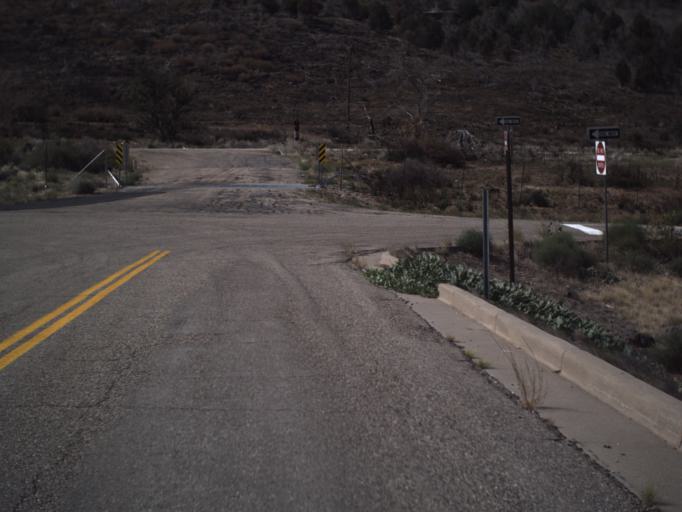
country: US
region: Utah
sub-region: Washington County
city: Toquerville
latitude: 37.3618
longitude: -113.2628
